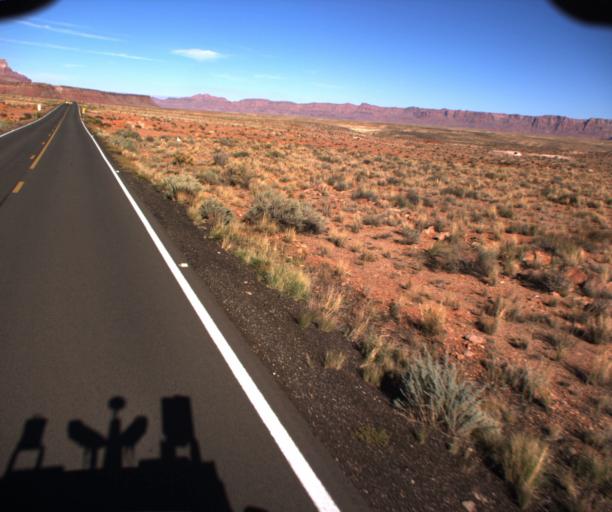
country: US
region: Arizona
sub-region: Coconino County
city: LeChee
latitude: 36.7057
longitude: -111.7857
